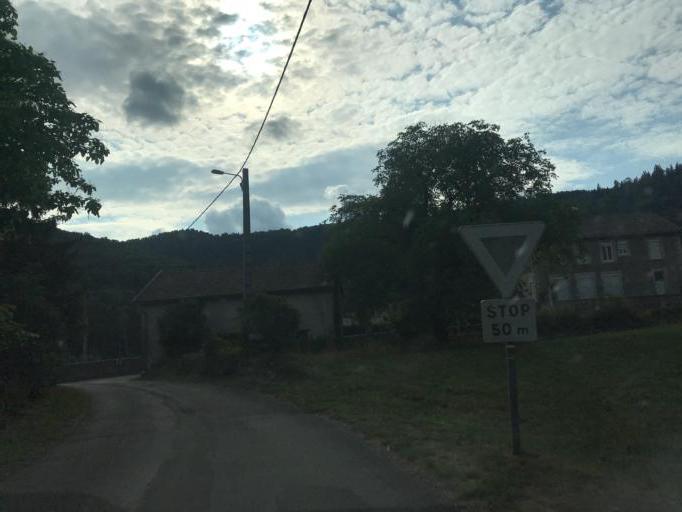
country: FR
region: Franche-Comte
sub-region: Departement du Jura
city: Saint-Lupicin
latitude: 46.4272
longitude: 5.8035
